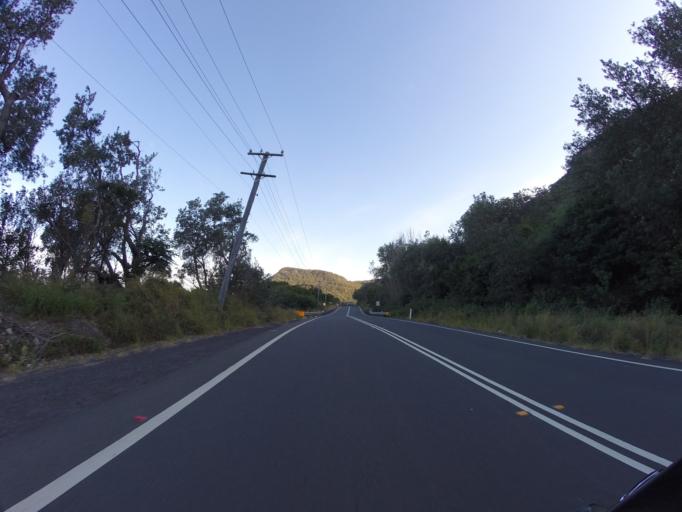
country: AU
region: New South Wales
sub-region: Wollongong
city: Helensburgh
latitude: -34.2394
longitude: 150.9816
